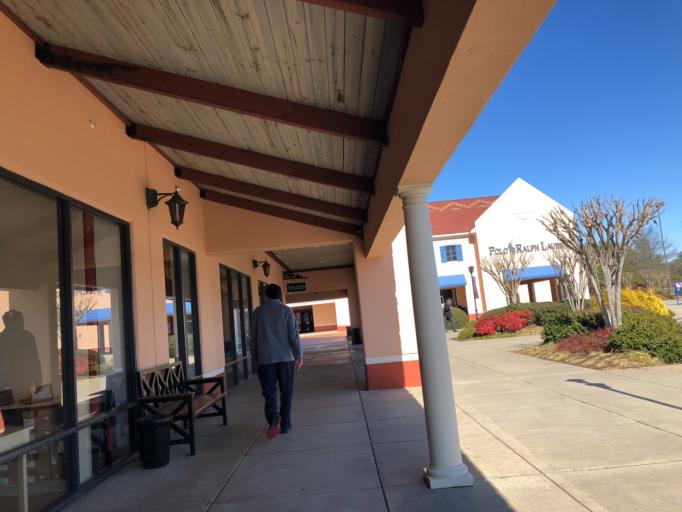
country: US
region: Georgia
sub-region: Dawson County
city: Dawsonville
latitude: 34.3584
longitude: -84.0467
